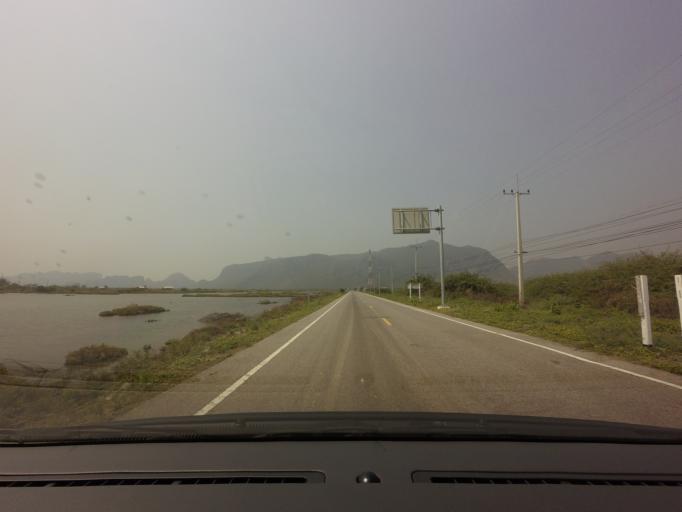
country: TH
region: Prachuap Khiri Khan
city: Sam Roi Yot
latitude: 12.1689
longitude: 99.9905
